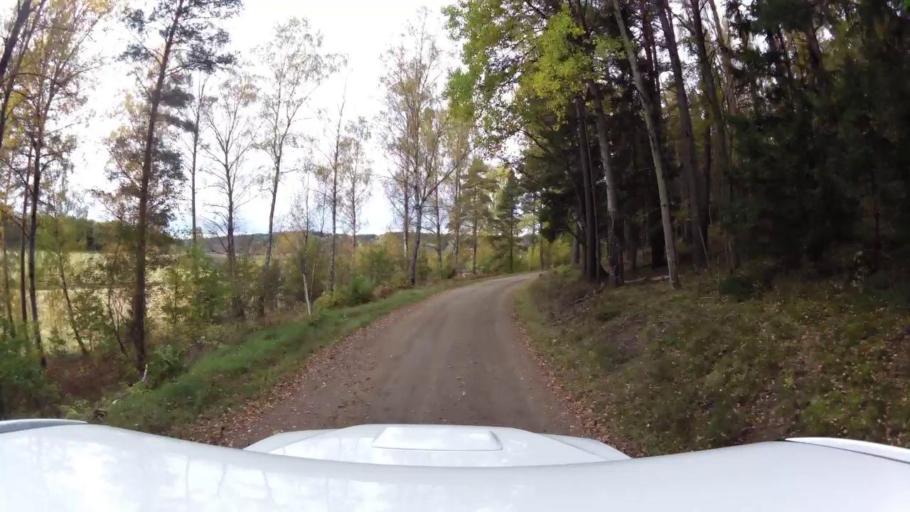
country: SE
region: OEstergoetland
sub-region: Linkopings Kommun
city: Ekangen
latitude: 58.5582
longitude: 15.6690
